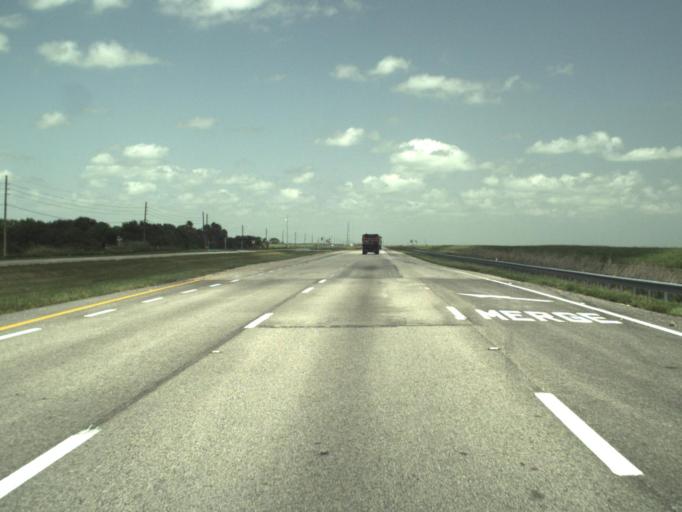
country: US
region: Florida
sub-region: Palm Beach County
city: Belle Glade Camp
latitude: 26.4879
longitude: -80.6561
